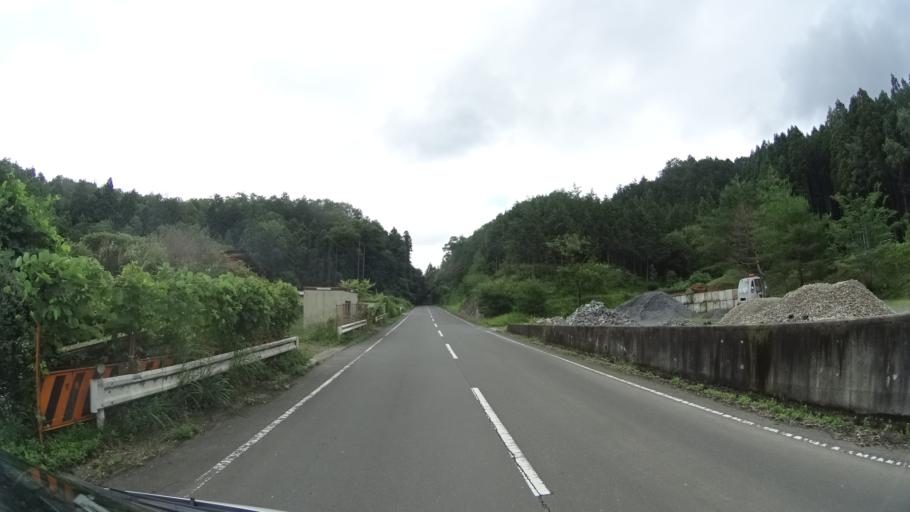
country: JP
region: Kyoto
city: Kameoka
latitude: 35.0913
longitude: 135.4320
